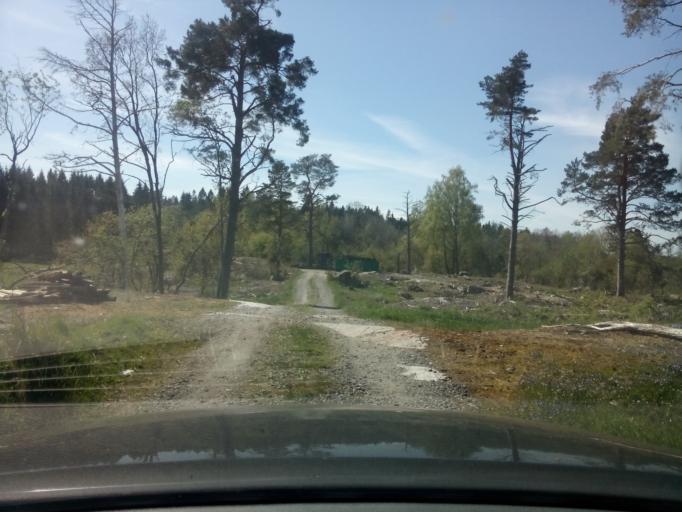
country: SE
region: Soedermanland
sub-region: Trosa Kommun
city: Trosa
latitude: 58.7958
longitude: 17.3768
